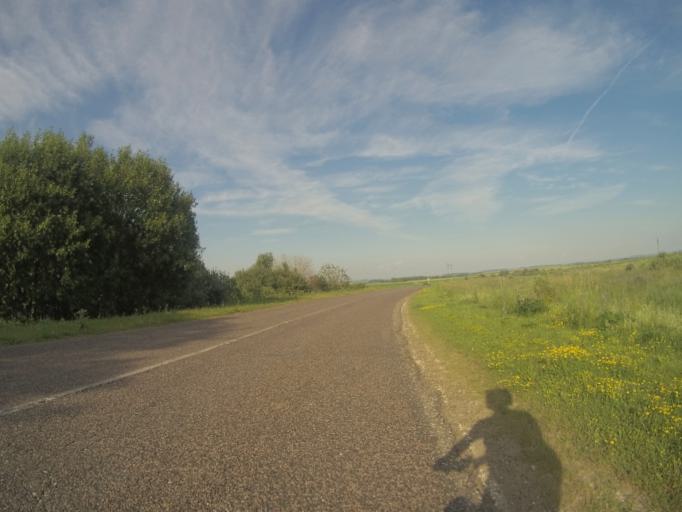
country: RU
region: Vladimir
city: Suzdal'
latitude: 56.3152
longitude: 40.2453
